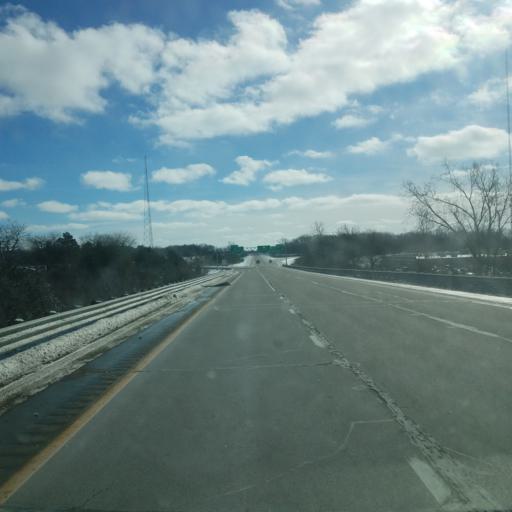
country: US
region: Michigan
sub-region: Ingham County
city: Holt
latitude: 42.6817
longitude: -84.5004
